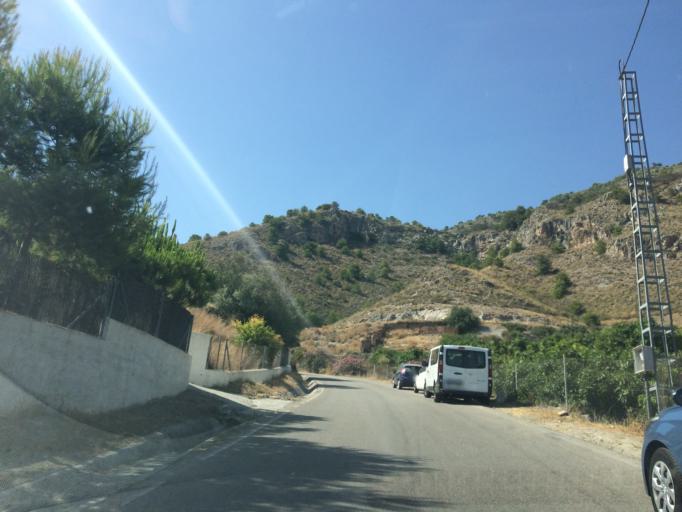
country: ES
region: Andalusia
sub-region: Provincia de Malaga
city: Frigiliana
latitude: 36.7965
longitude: -3.9015
